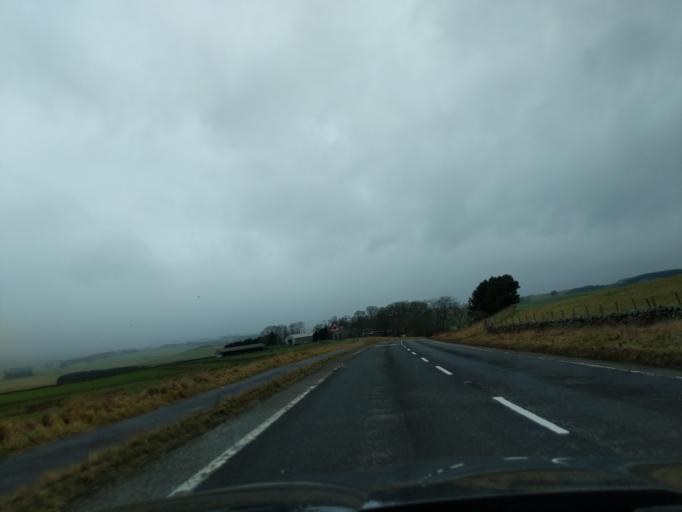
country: GB
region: England
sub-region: Northumberland
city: Otterburn
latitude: 55.2186
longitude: -2.1330
